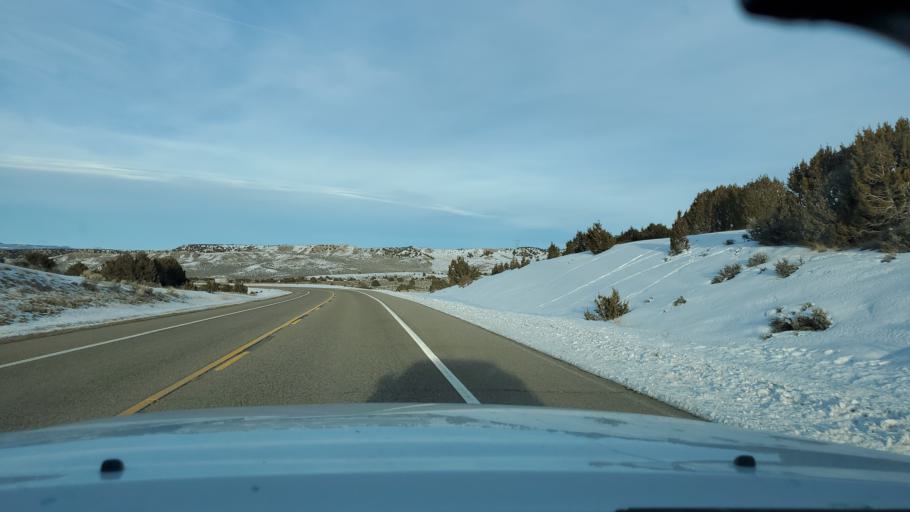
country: US
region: Colorado
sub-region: Rio Blanco County
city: Rangely
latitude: 40.3857
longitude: -108.3496
